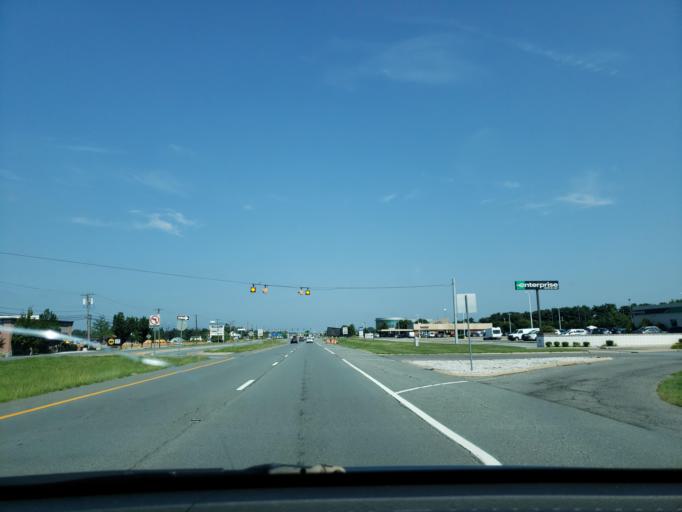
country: US
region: Delaware
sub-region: Kent County
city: Dover
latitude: 39.1510
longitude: -75.5045
